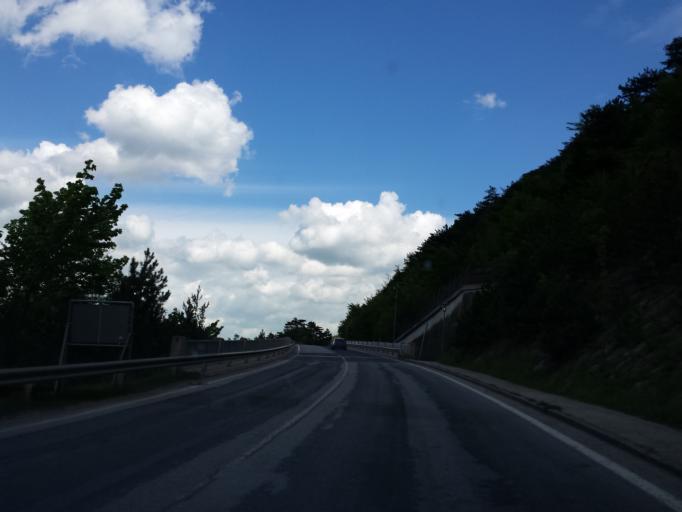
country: AT
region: Lower Austria
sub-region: Politischer Bezirk Wiener Neustadt
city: Waldegg
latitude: 47.8674
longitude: 16.0553
